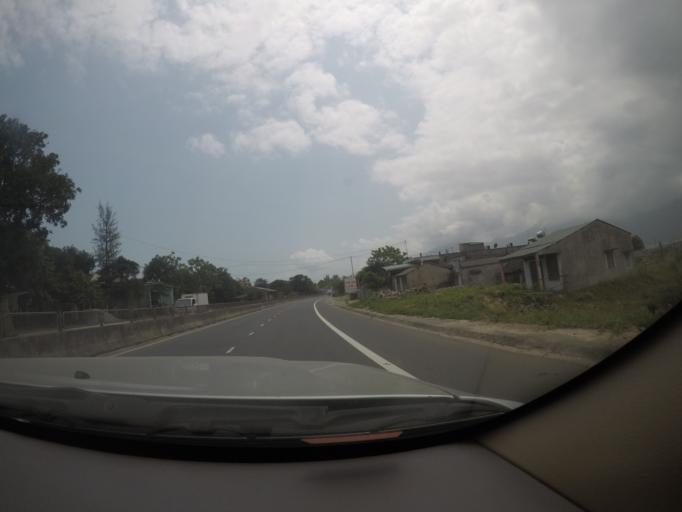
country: VN
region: Thua Thien-Hue
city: Phu Loc
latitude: 16.2629
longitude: 108.0569
